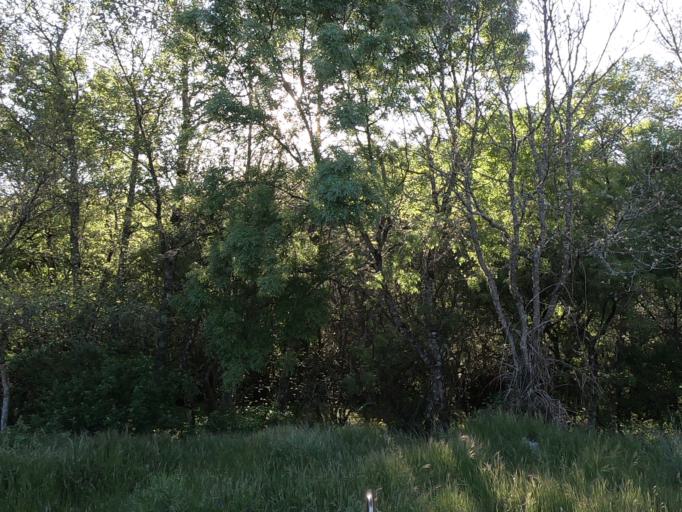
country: PT
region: Vila Real
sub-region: Vila Real
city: Vila Real
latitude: 41.3356
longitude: -7.6701
